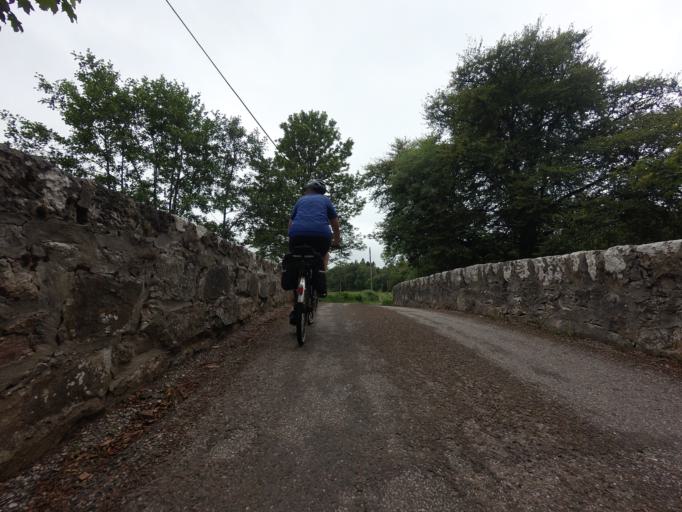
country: GB
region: Scotland
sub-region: Highland
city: Evanton
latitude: 57.9847
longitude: -4.4190
